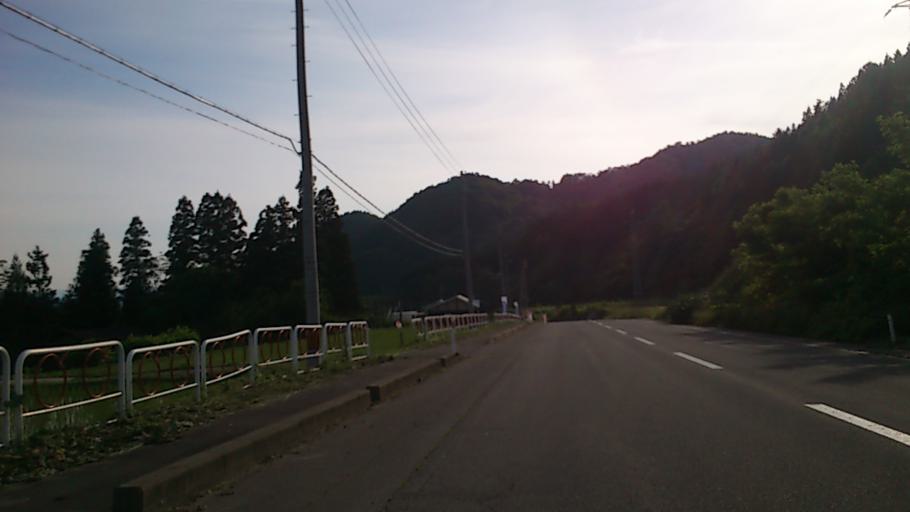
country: JP
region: Aomori
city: Kuroishi
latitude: 40.6352
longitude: 140.7173
